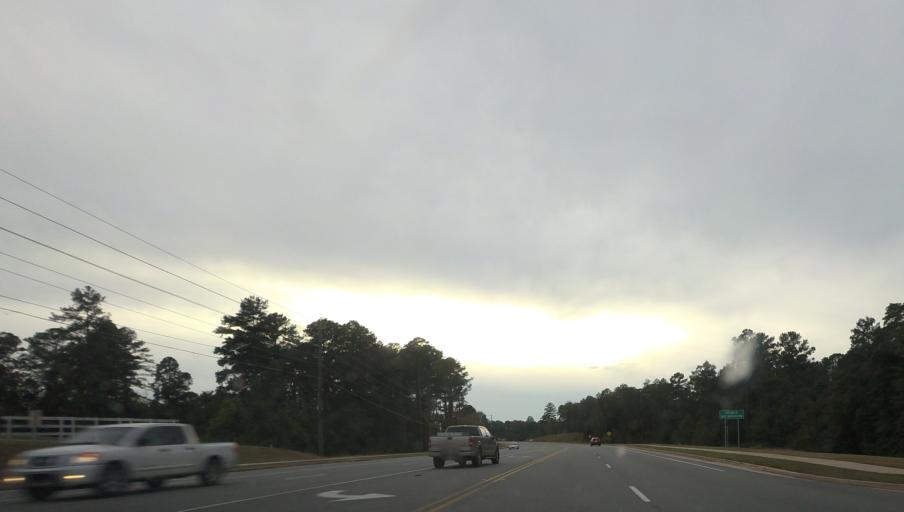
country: US
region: Georgia
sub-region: Houston County
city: Perry
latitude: 32.4975
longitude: -83.6728
